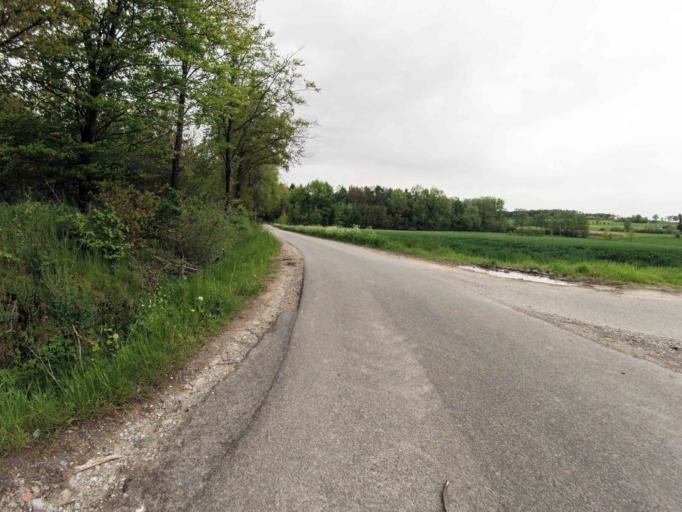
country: DE
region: Lower Saxony
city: Bad Essen
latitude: 52.3125
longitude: 8.3004
